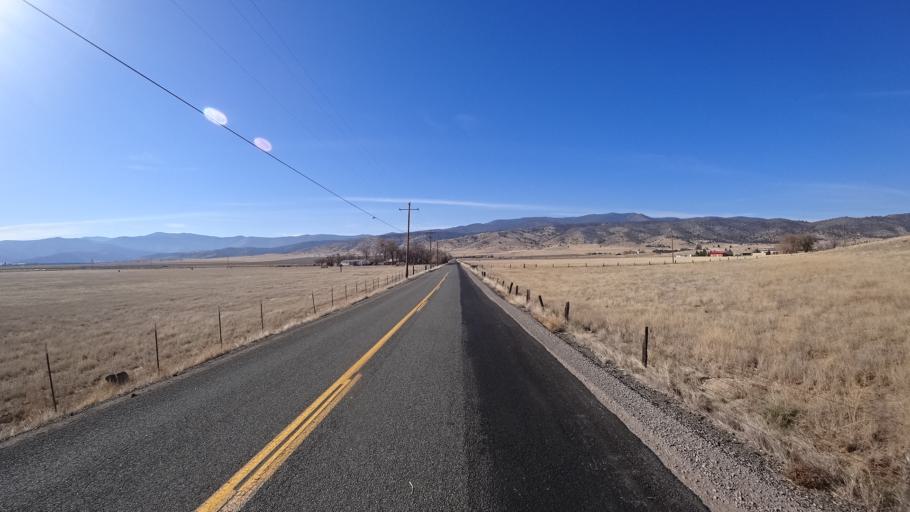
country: US
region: California
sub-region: Siskiyou County
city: Montague
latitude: 41.5746
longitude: -122.5334
